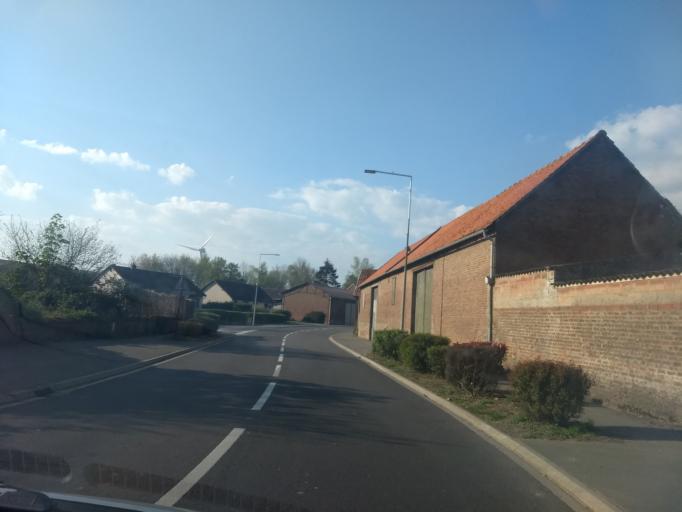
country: FR
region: Nord-Pas-de-Calais
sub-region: Departement du Pas-de-Calais
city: Bucquoy
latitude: 50.1361
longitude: 2.7073
